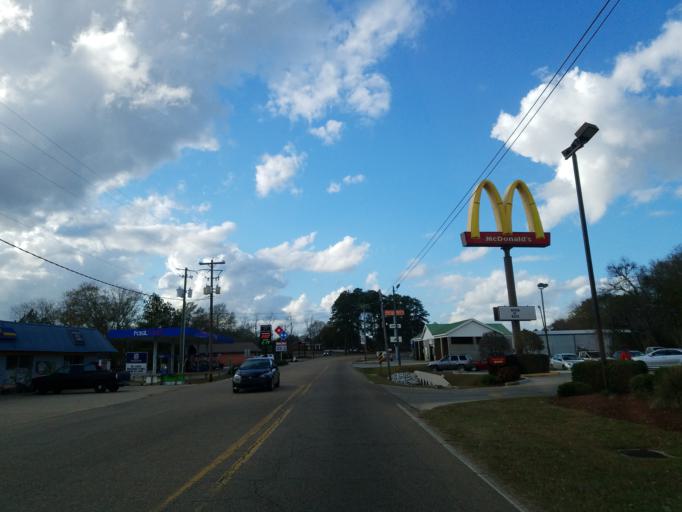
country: US
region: Mississippi
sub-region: Jones County
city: Ellisville
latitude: 31.6086
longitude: -89.2025
